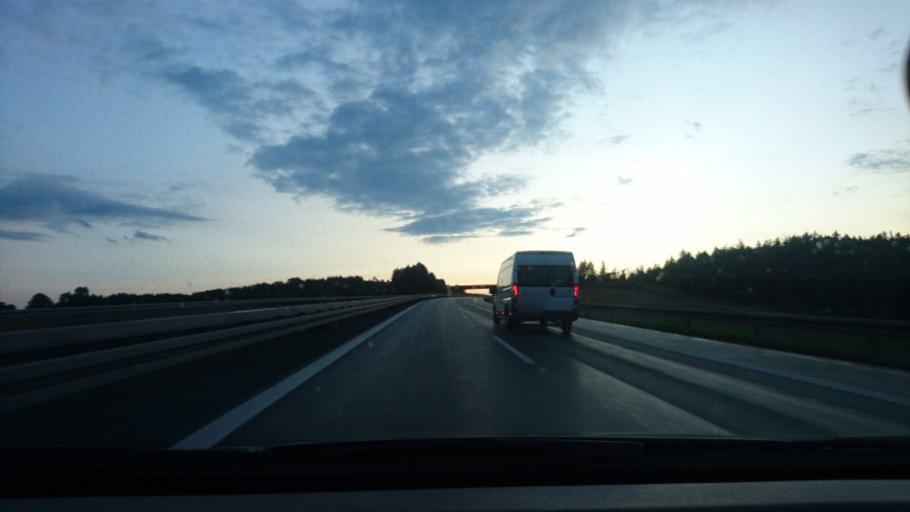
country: DE
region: Bavaria
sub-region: Upper Franconia
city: Feilitzsch
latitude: 50.3758
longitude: 11.9344
